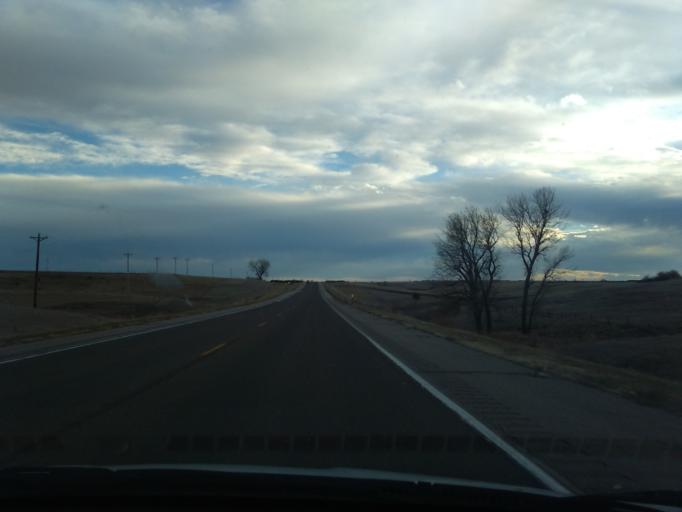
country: US
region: Nebraska
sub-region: Phelps County
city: Holdrege
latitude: 40.3541
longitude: -99.3689
